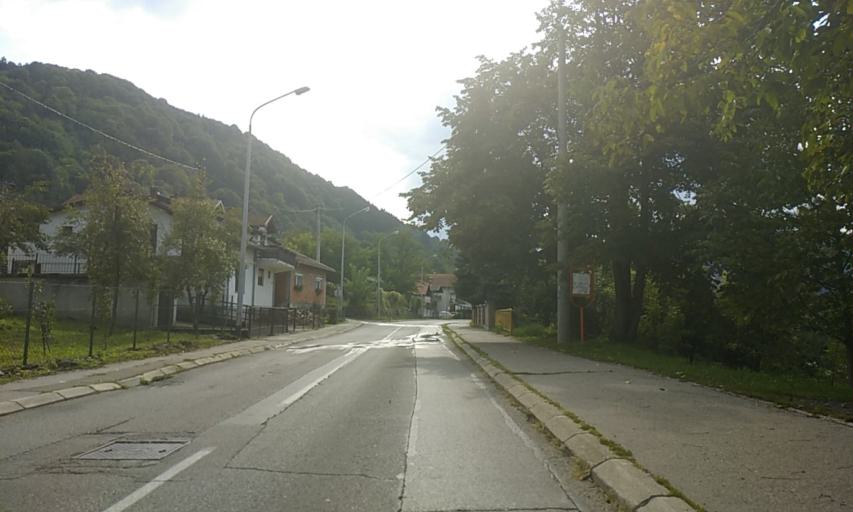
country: BA
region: Republika Srpska
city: Hiseti
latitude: 44.7518
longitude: 17.1745
